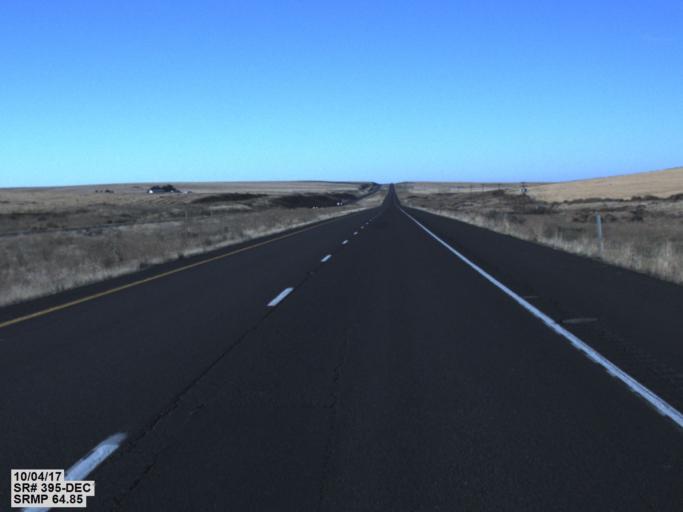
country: US
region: Washington
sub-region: Franklin County
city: Connell
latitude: 46.7764
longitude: -118.7724
